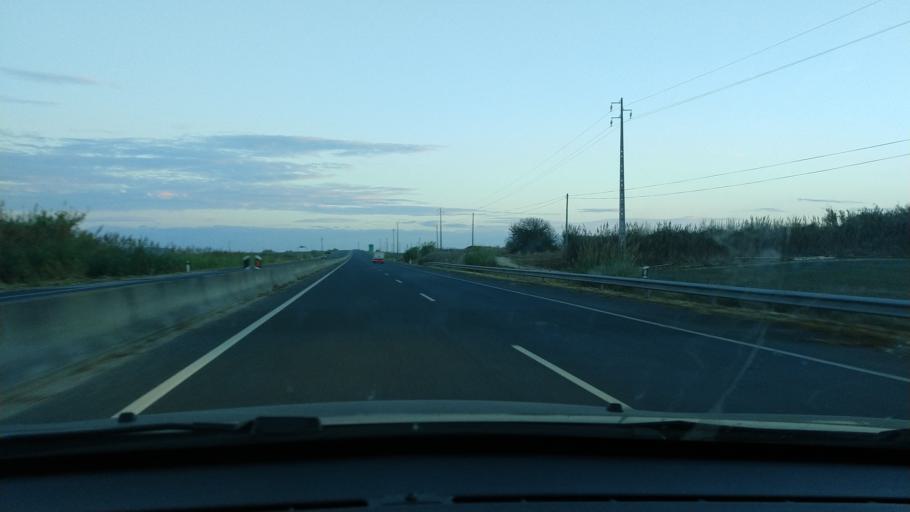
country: PT
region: Leiria
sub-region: Peniche
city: Atouguia da Baleia
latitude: 39.3399
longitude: -9.3383
